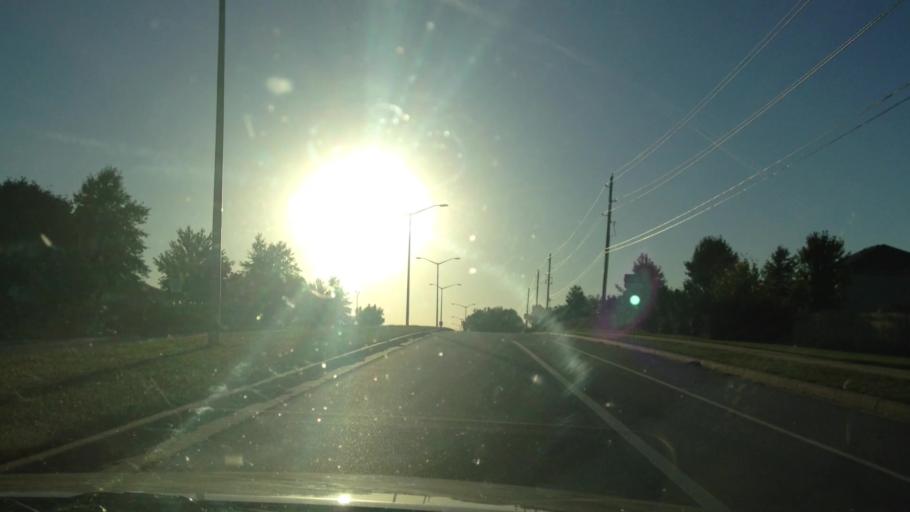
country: US
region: Missouri
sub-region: Clay County
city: Pleasant Valley
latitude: 39.2885
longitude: -94.4843
